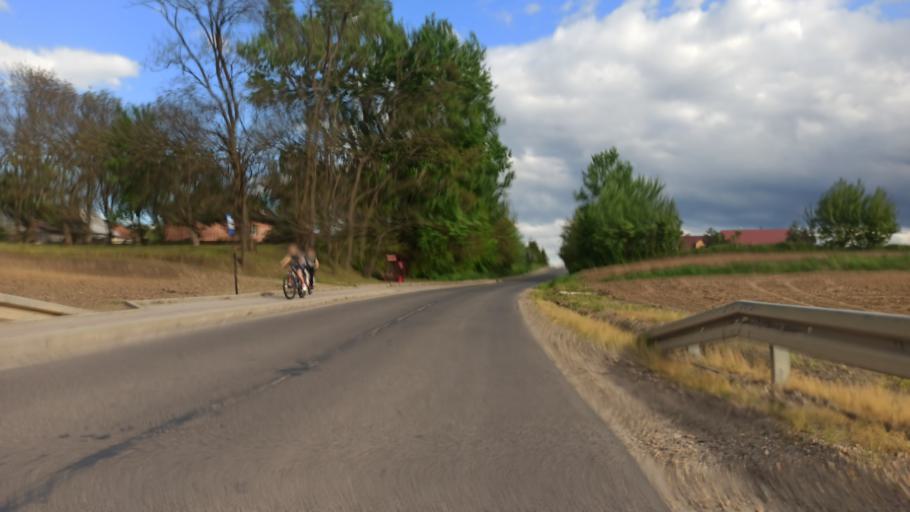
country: PL
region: Subcarpathian Voivodeship
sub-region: Powiat jaroslawski
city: Sosnica
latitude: 49.9188
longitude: 22.8575
